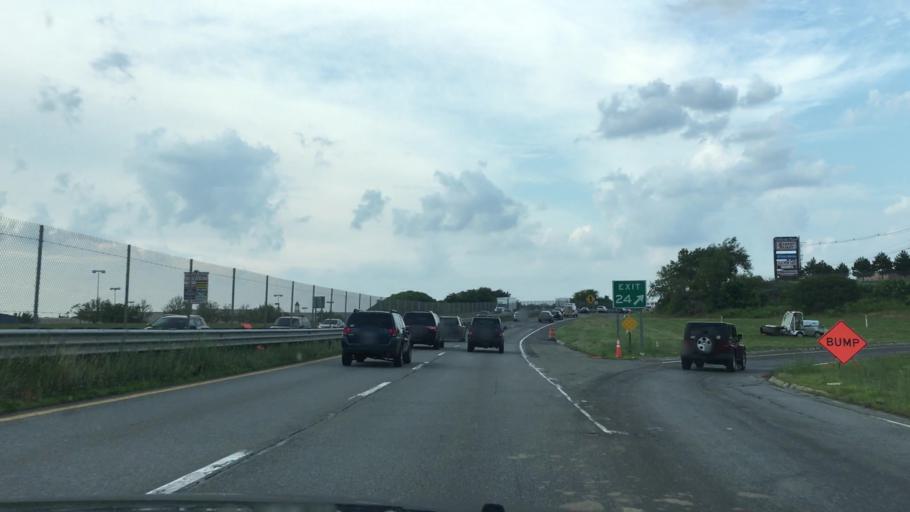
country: US
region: Massachusetts
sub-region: Essex County
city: Peabody
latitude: 42.5497
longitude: -70.9365
